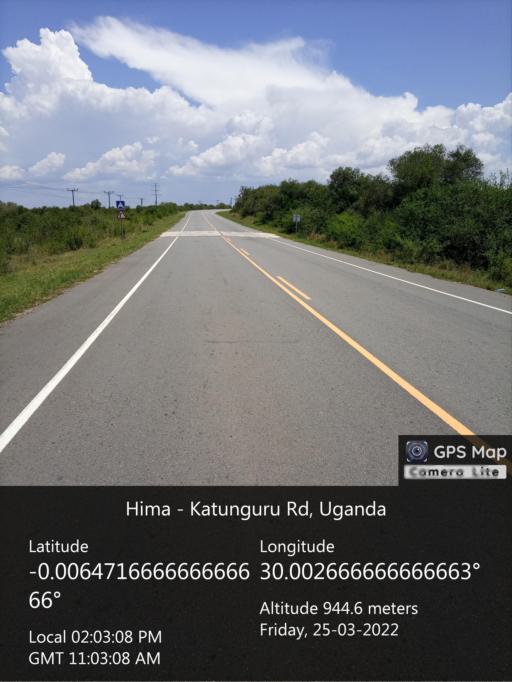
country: UG
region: Western Region
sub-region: Kasese District
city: Kilembe
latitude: -0.0065
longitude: 30.0027
